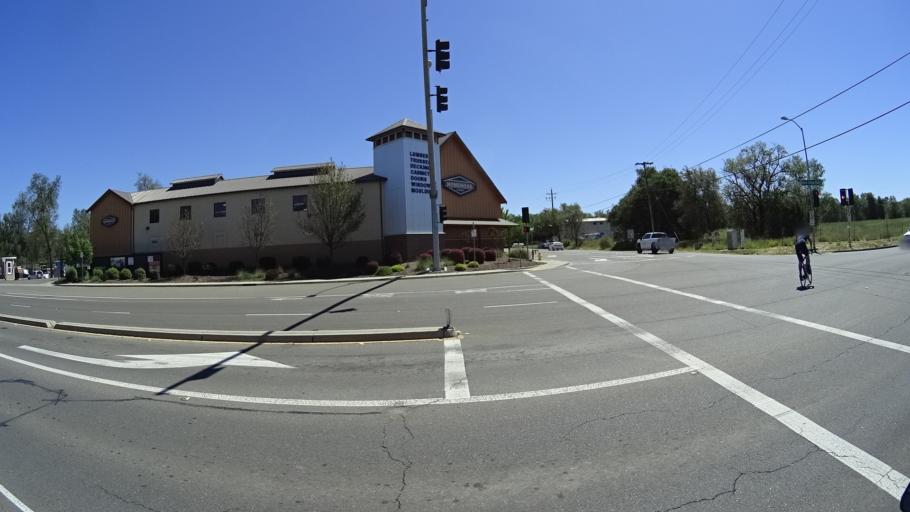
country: US
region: California
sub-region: Placer County
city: Loomis
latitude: 38.8105
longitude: -121.2056
